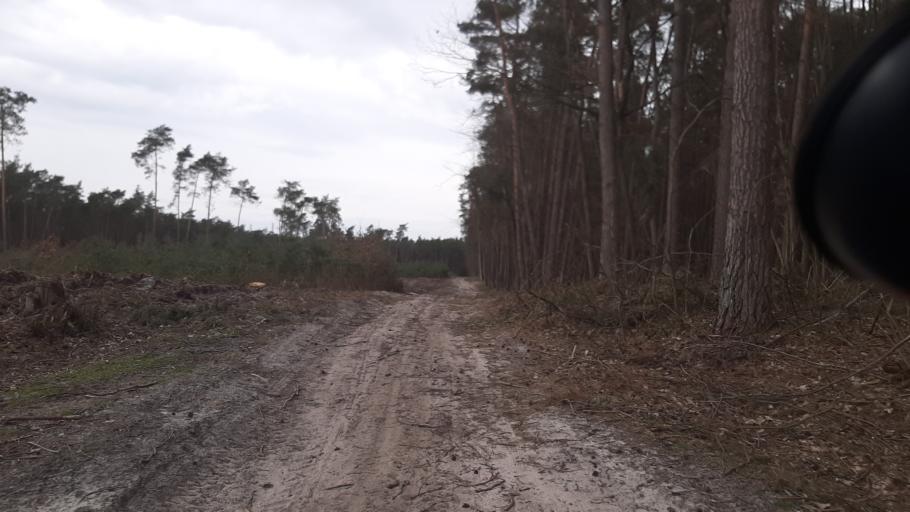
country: PL
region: Lublin Voivodeship
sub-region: Powiat lubelski
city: Garbow
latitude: 51.3959
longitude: 22.3770
